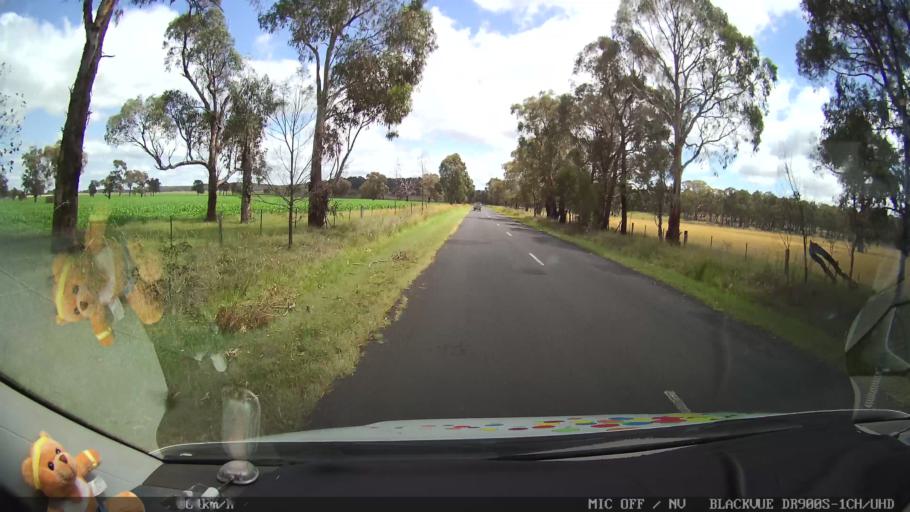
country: AU
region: New South Wales
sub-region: Glen Innes Severn
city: Glen Innes
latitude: -29.6036
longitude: 151.6667
